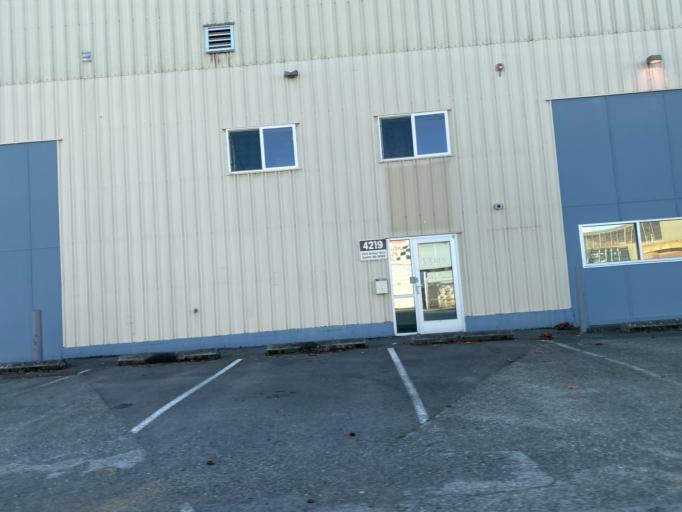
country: US
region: Washington
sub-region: King County
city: Seattle
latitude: 47.6584
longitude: -122.3847
